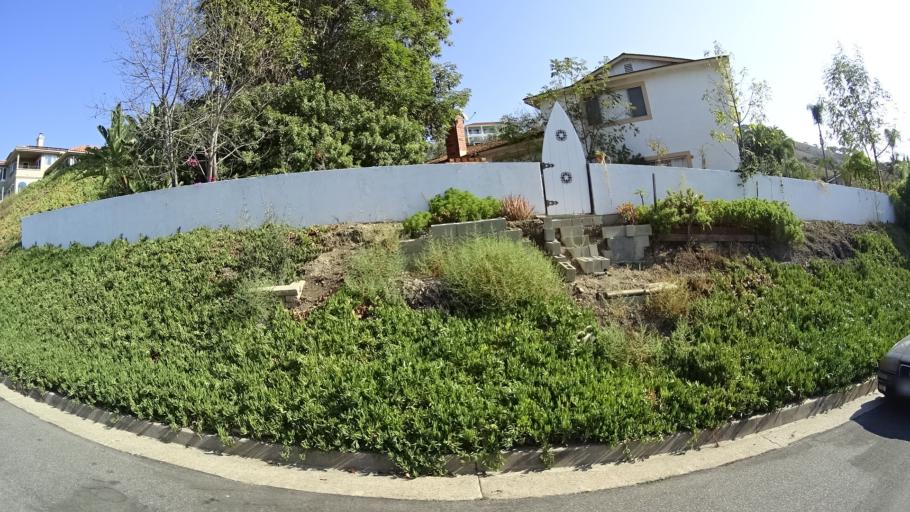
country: US
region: California
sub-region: Orange County
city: San Juan Capistrano
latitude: 33.4651
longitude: -117.6558
